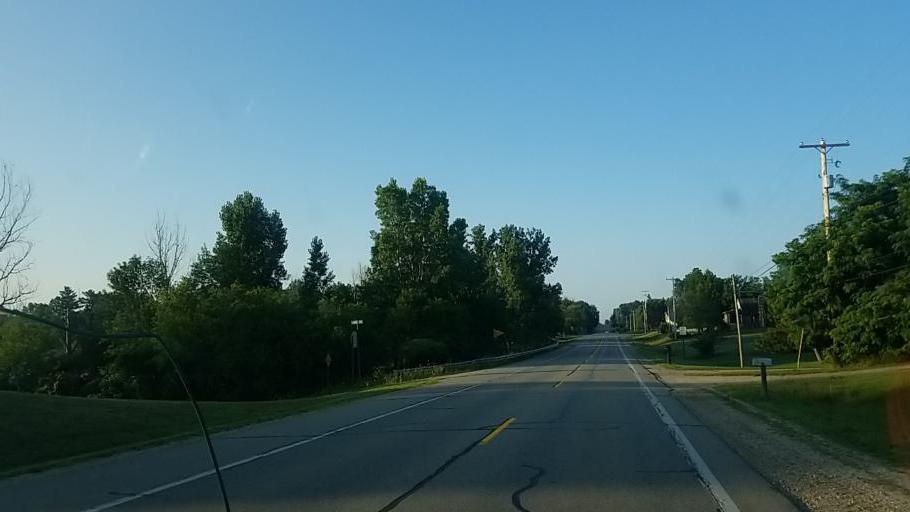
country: US
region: Michigan
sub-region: Montcalm County
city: Edmore
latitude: 43.4394
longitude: -85.1490
